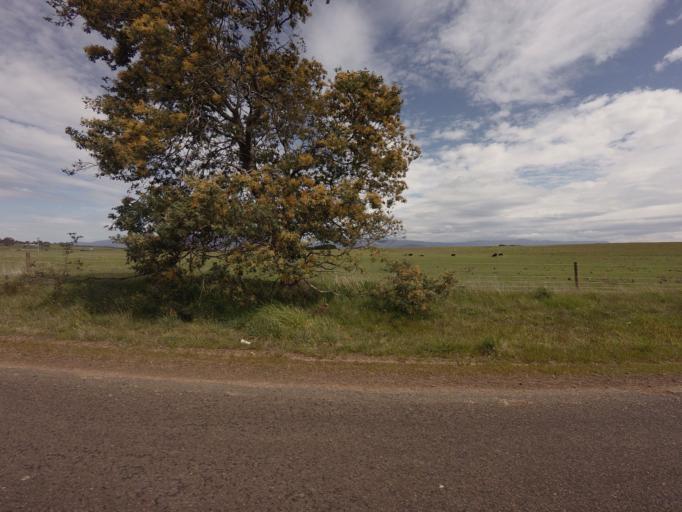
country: AU
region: Tasmania
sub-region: Northern Midlands
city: Longford
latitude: -41.7794
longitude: 147.2300
